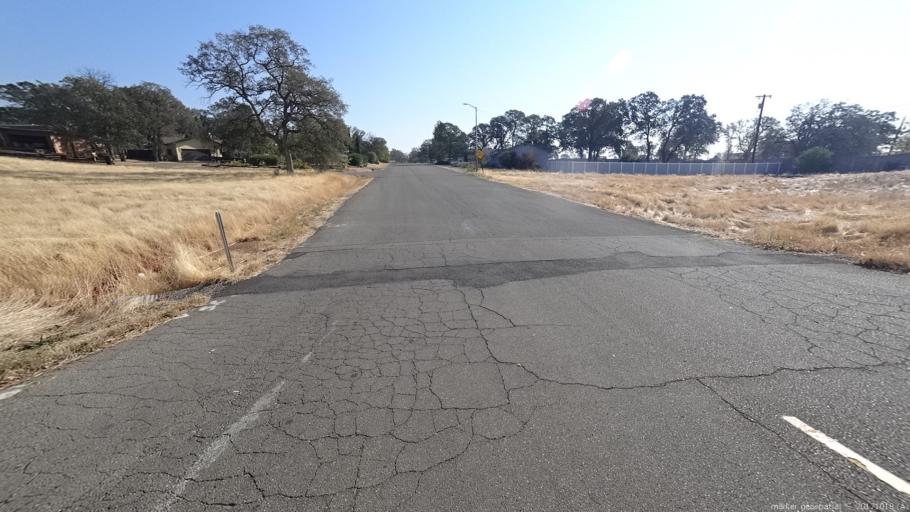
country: US
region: California
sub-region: Shasta County
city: Palo Cedro
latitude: 40.5471
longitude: -122.3026
